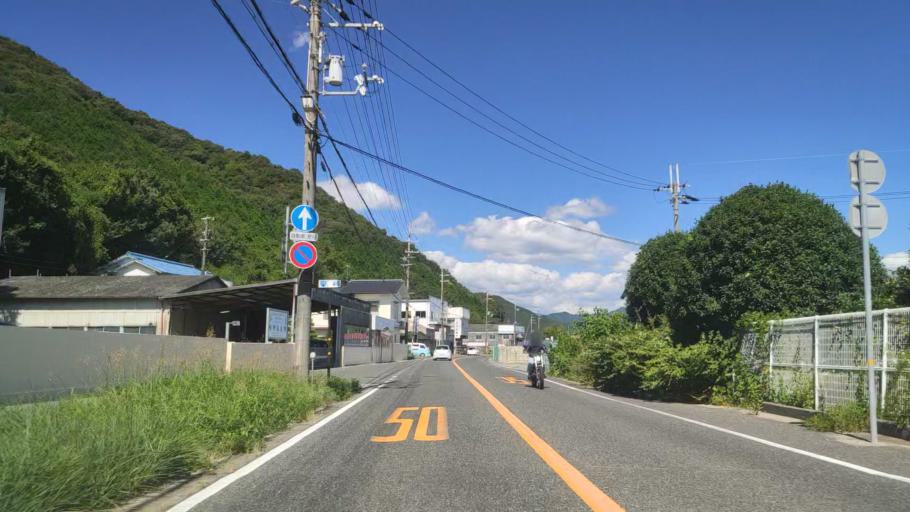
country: JP
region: Hyogo
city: Nishiwaki
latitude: 35.0141
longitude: 134.9892
